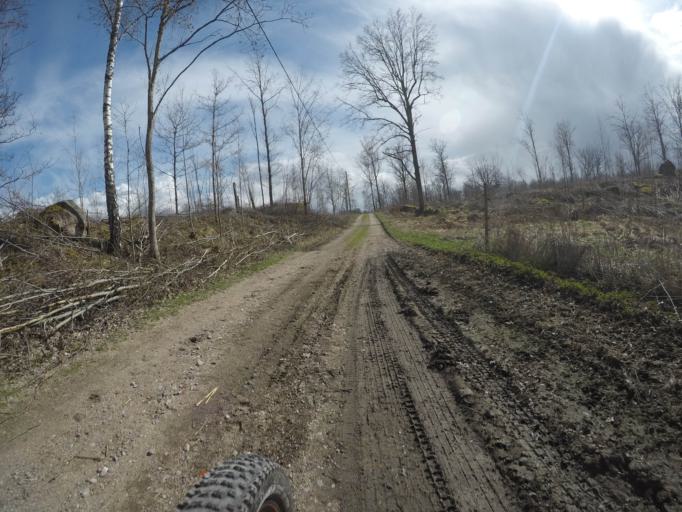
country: SE
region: Vaestmanland
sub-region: Kungsors Kommun
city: Kungsoer
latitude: 59.2765
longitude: 16.1530
